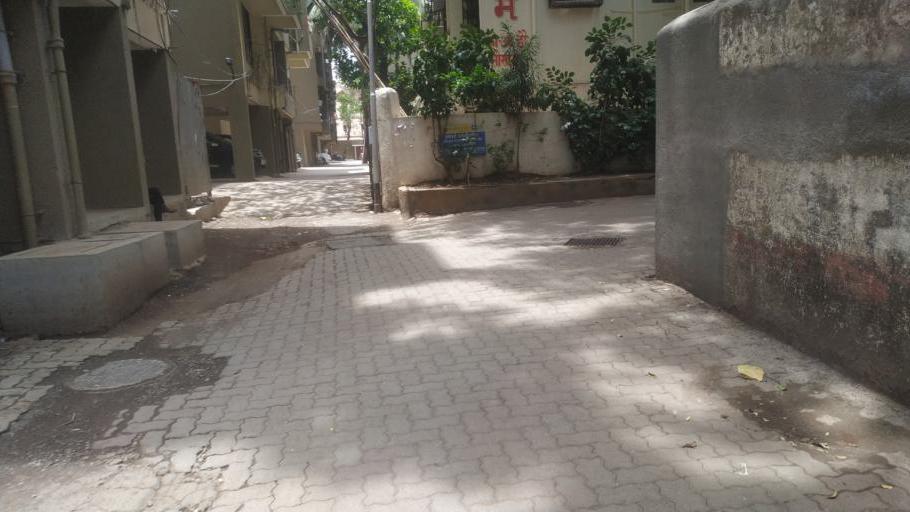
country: IN
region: Maharashtra
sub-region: Mumbai Suburban
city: Mumbai
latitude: 18.9929
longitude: 72.8382
